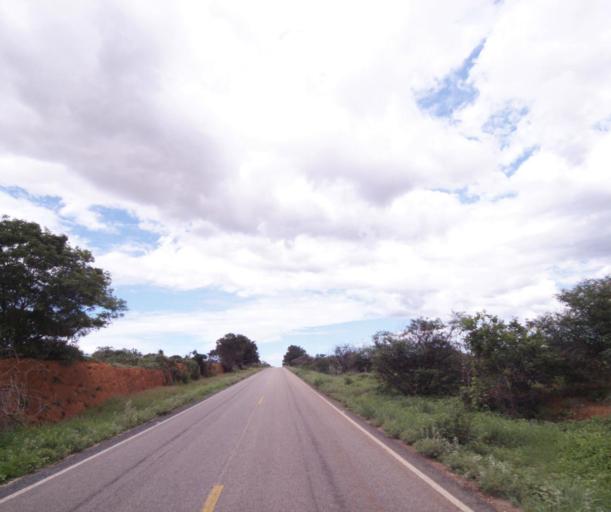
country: BR
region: Bahia
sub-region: Palmas De Monte Alto
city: Palmas de Monte Alto
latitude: -14.2598
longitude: -43.2886
